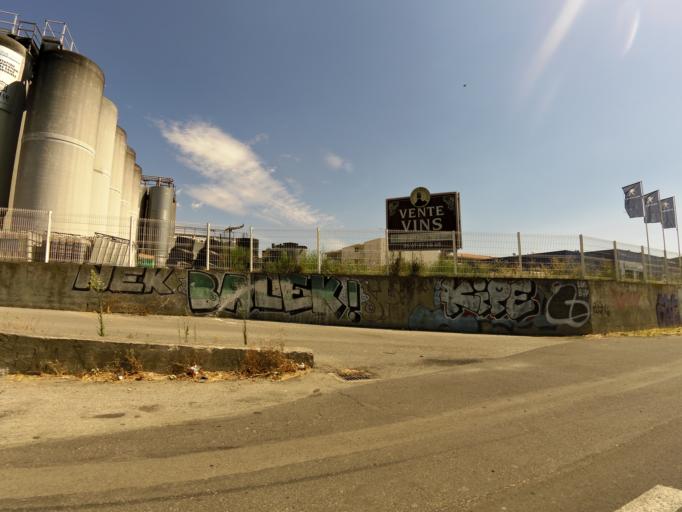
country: FR
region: Languedoc-Roussillon
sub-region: Departement de l'Herault
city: Vendargues
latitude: 43.6529
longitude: 3.9723
